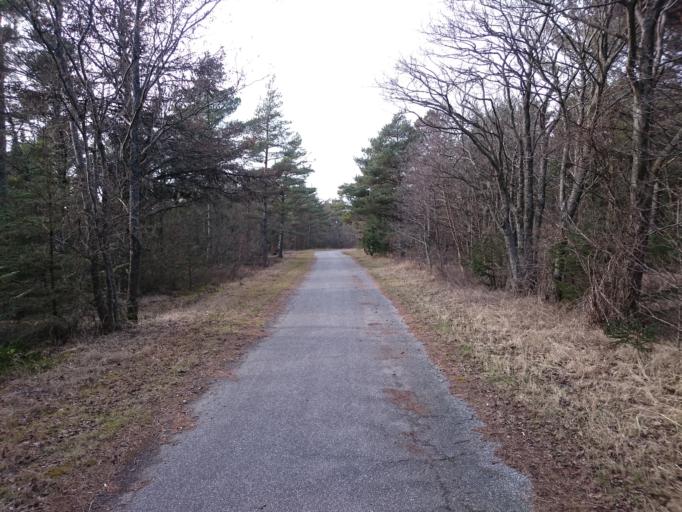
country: DK
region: North Denmark
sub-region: Frederikshavn Kommune
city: Skagen
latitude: 57.6991
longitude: 10.5197
